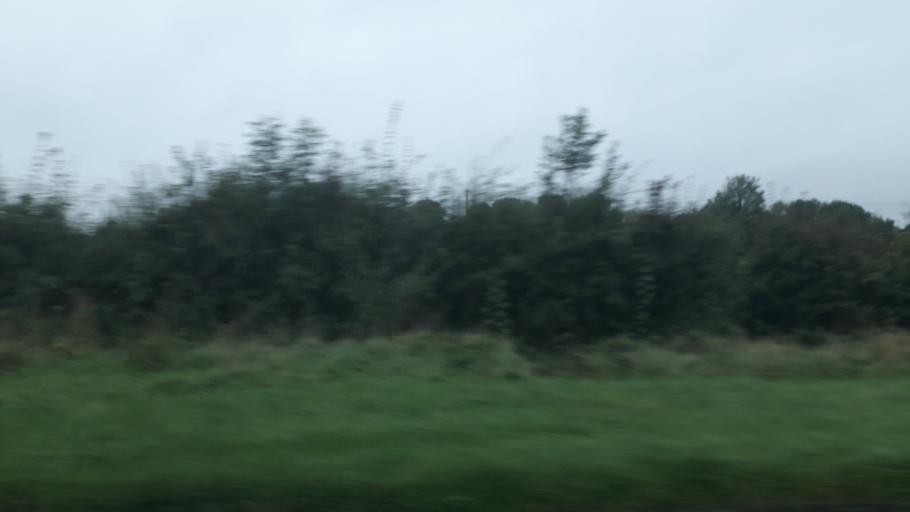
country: IE
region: Leinster
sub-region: An Longfort
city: Edgeworthstown
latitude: 53.6509
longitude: -7.5128
